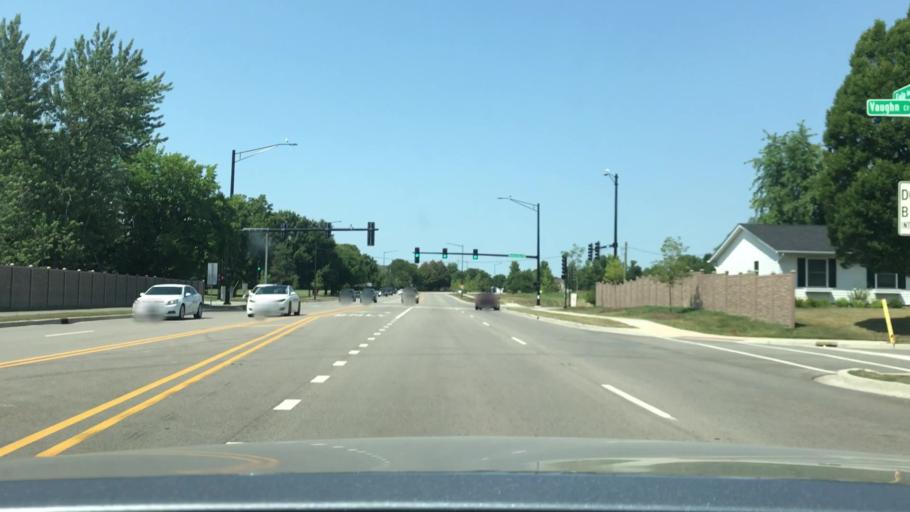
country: US
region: Illinois
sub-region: Kane County
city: Aurora
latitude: 41.7312
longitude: -88.2534
